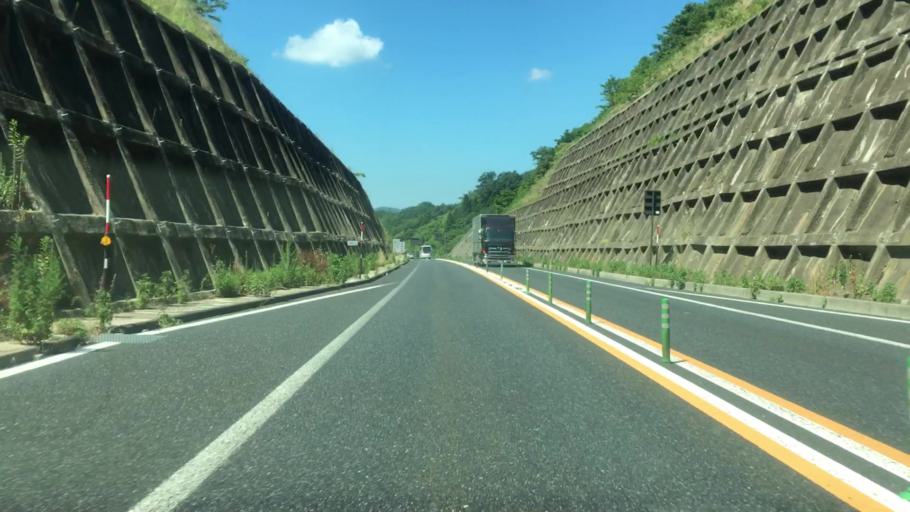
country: JP
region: Tottori
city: Tottori
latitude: 35.3600
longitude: 134.1997
